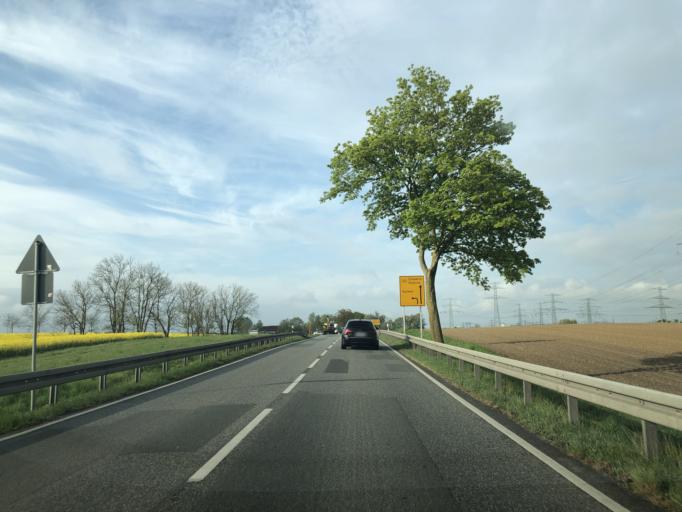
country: DE
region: Mecklenburg-Vorpommern
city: Guestrow
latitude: 53.8233
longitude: 12.2012
